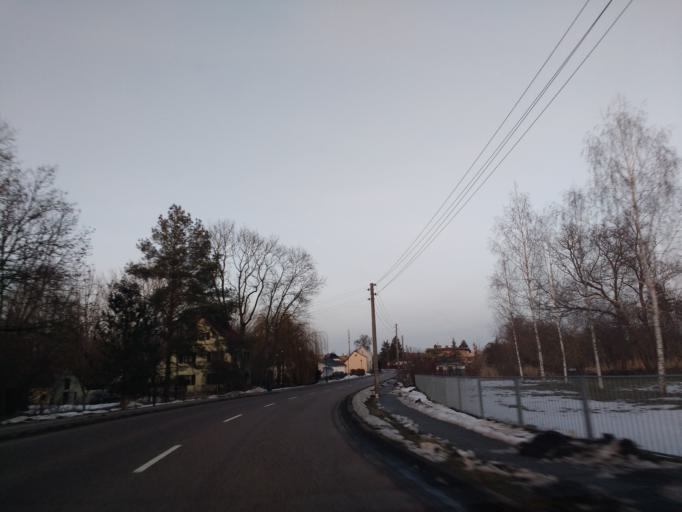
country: DE
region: Saxony-Anhalt
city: Sennewitz
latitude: 51.5391
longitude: 11.9555
